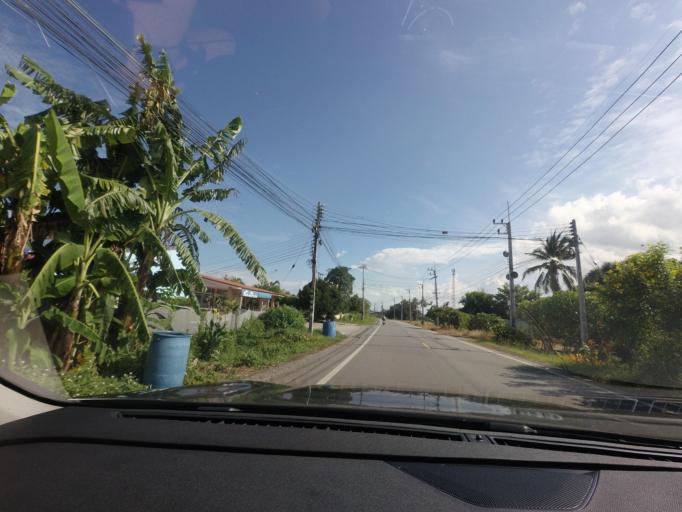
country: TH
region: Prachuap Khiri Khan
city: Pran Buri
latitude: 12.4364
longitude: 99.9447
